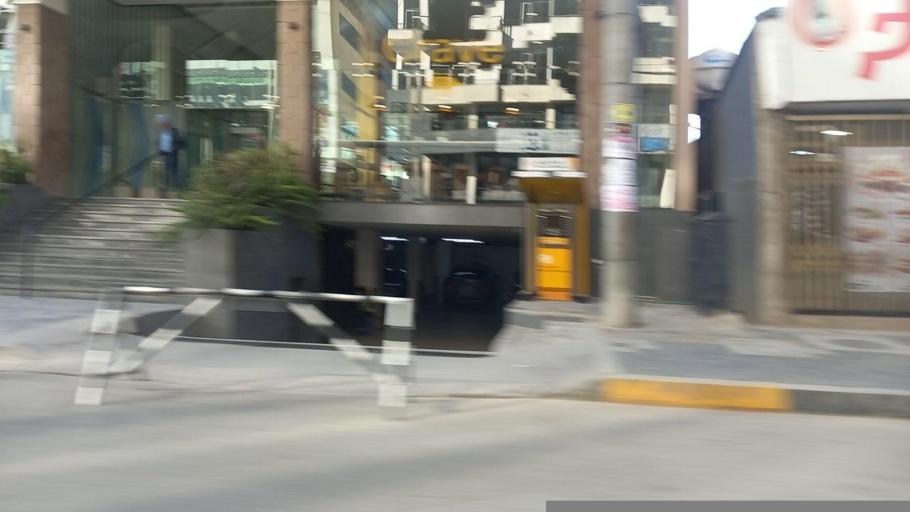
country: ET
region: Adis Abeba
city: Addis Ababa
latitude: 9.0013
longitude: 38.7672
